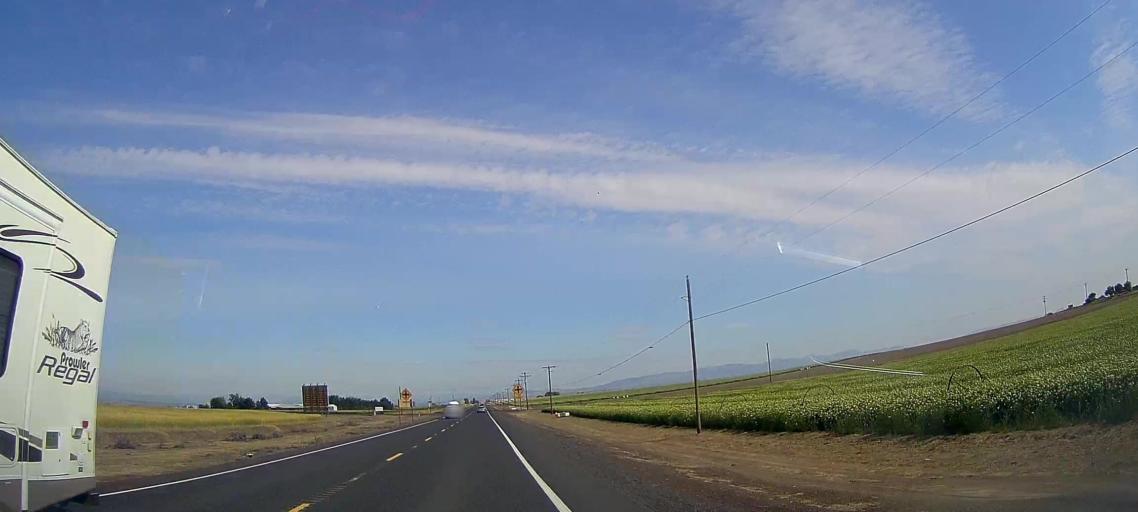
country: US
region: Oregon
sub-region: Jefferson County
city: Madras
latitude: 44.6776
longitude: -121.1453
